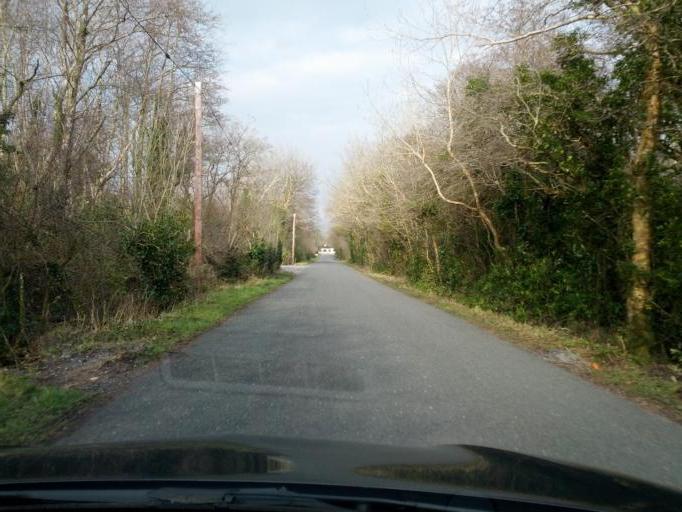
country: IE
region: Connaught
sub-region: County Galway
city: Loughrea
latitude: 53.4715
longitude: -8.5238
